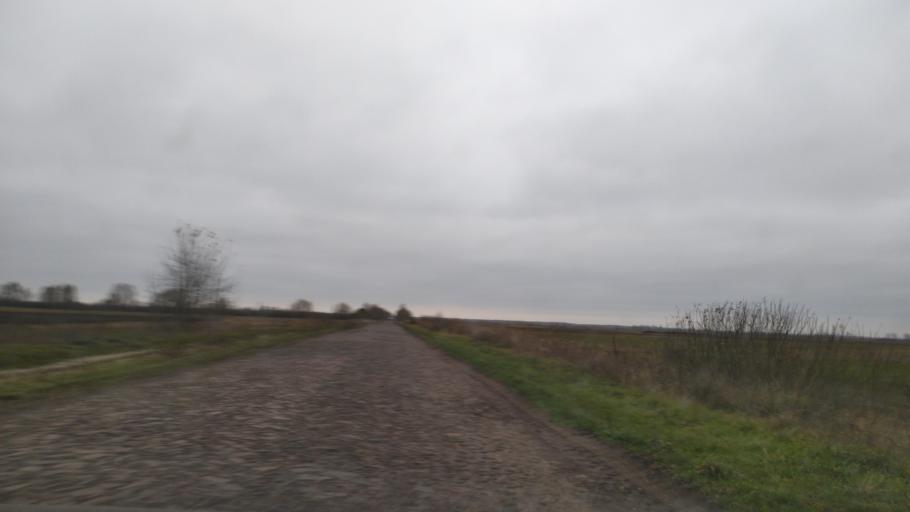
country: BY
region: Brest
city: Davyd-Haradok
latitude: 52.0063
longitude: 27.2055
